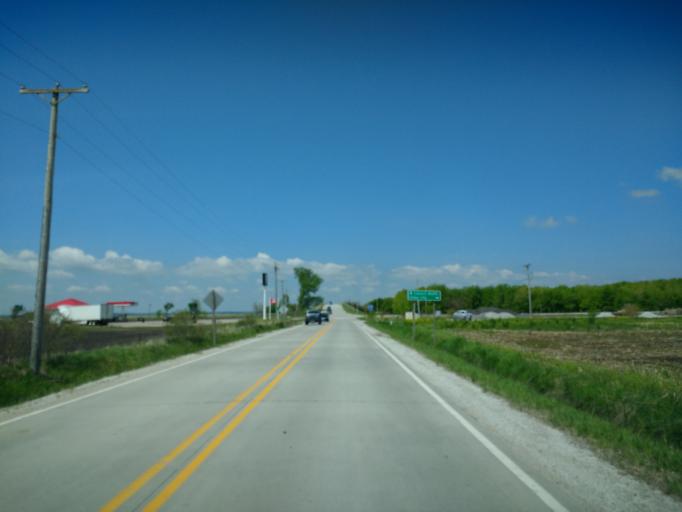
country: US
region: Iowa
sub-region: Harrison County
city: Missouri Valley
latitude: 41.4993
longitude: -95.8972
